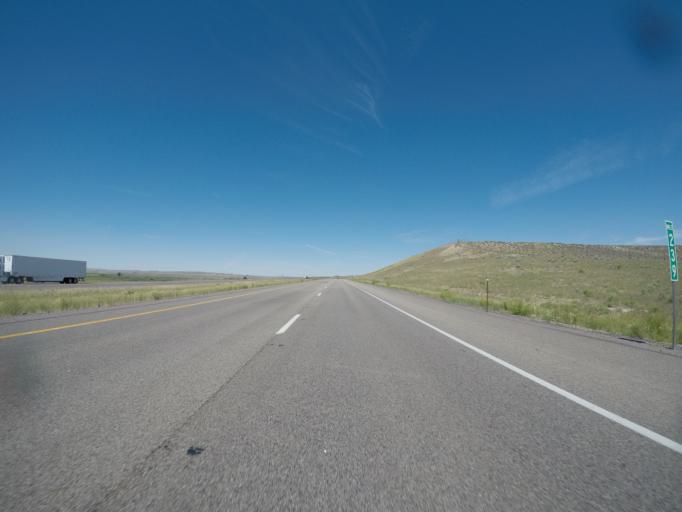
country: US
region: Wyoming
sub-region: Carbon County
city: Saratoga
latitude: 41.7402
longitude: -106.7583
